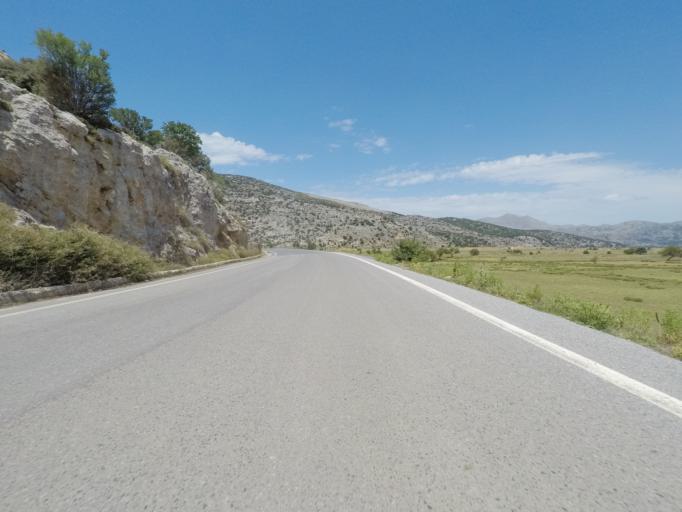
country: GR
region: Crete
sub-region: Nomos Irakleiou
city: Mokhos
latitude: 35.1893
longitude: 25.4318
